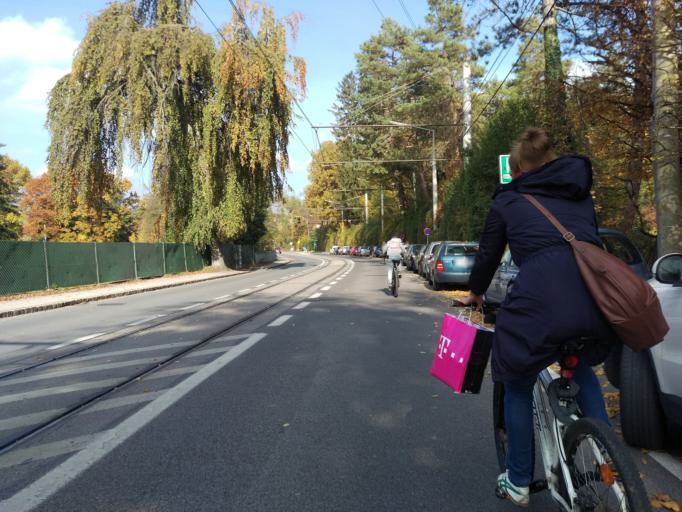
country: AT
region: Styria
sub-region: Graz Stadt
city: Graz
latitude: 47.0851
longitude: 15.4604
